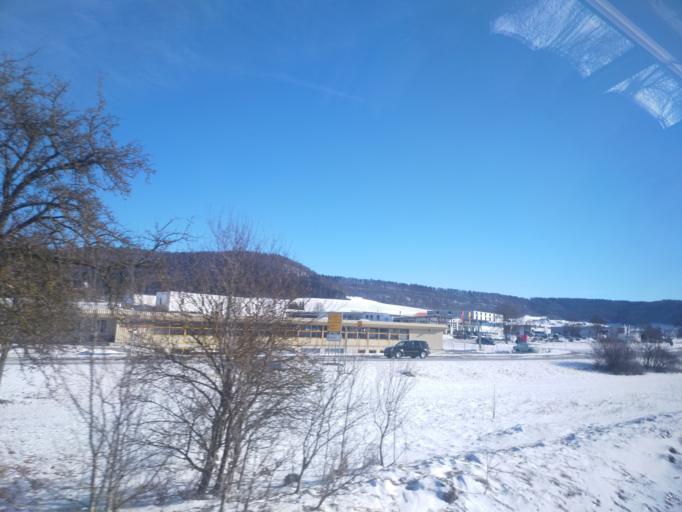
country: DE
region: Baden-Wuerttemberg
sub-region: Freiburg Region
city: Balgheim
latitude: 48.0633
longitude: 8.7650
